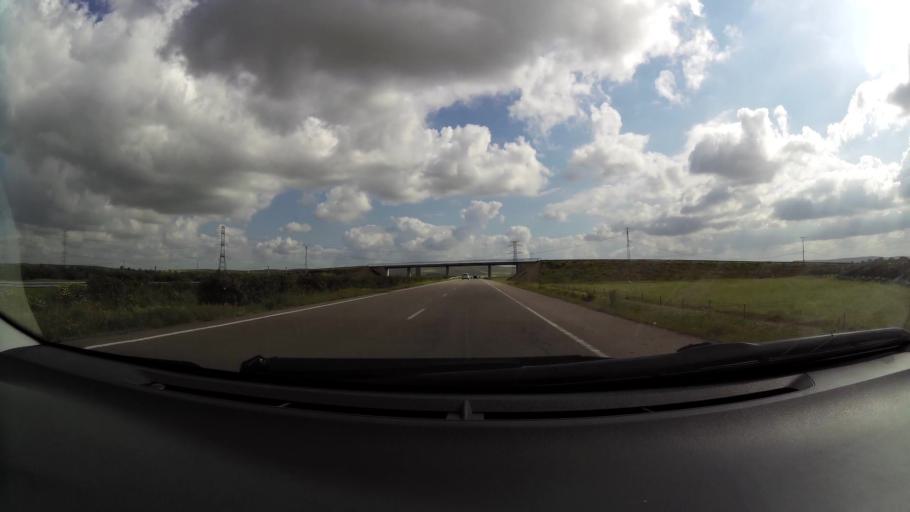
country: MA
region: Chaouia-Ouardigha
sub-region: Settat Province
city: Settat
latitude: 33.1145
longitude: -7.5814
